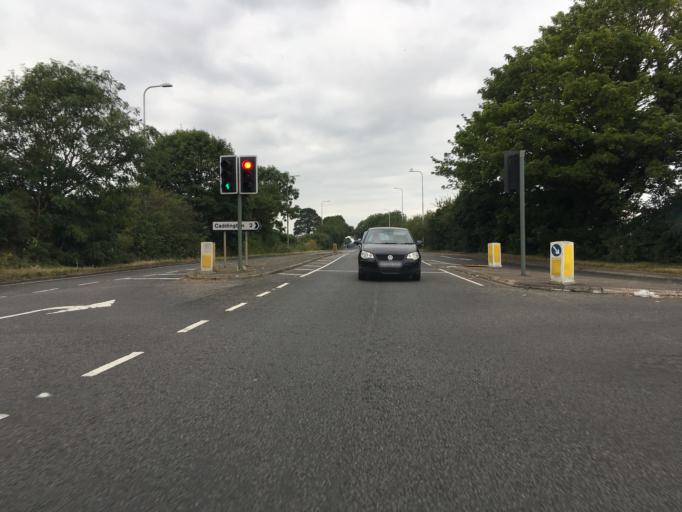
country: GB
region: England
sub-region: Central Bedfordshire
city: Kensworth
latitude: 51.8689
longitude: -0.4933
